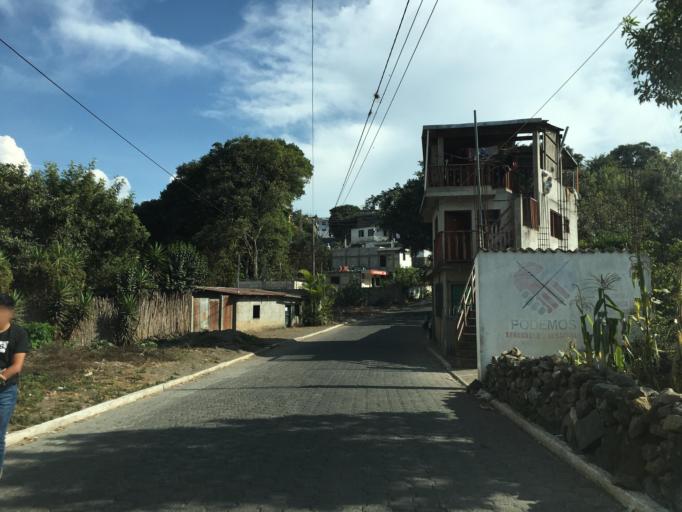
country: GT
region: Solola
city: Santa Catarina Palopo
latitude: 14.6680
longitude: -91.1667
